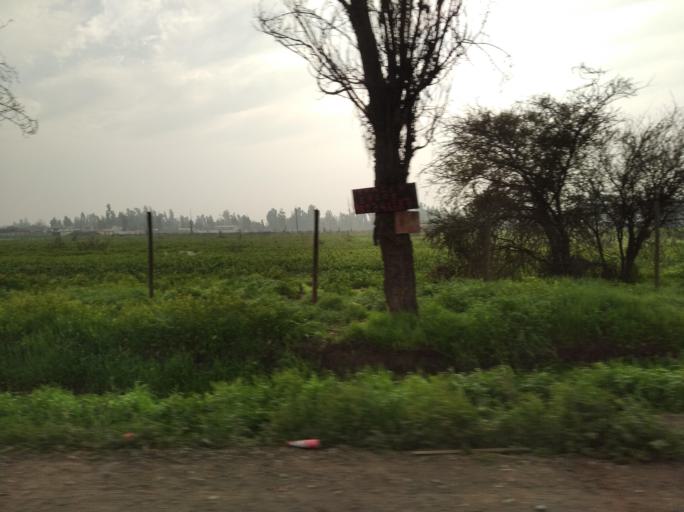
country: CL
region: Santiago Metropolitan
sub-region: Provincia de Chacabuco
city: Lampa
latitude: -33.3128
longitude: -70.8404
